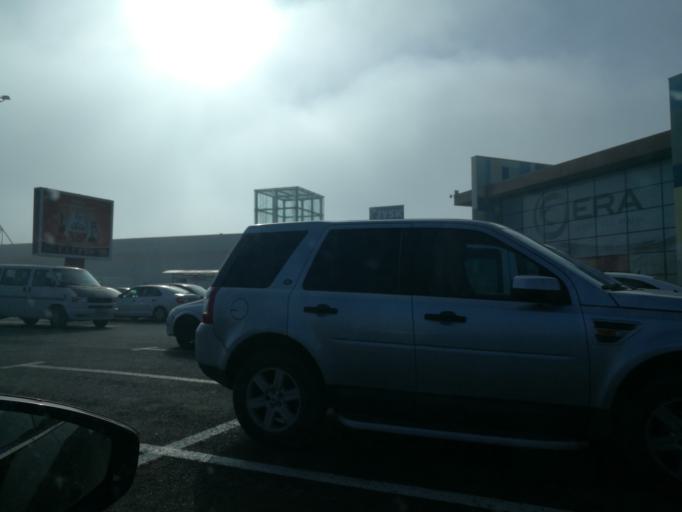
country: RO
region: Iasi
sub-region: Comuna Valea Lupului
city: Valea Lupului
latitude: 47.1678
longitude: 27.5116
